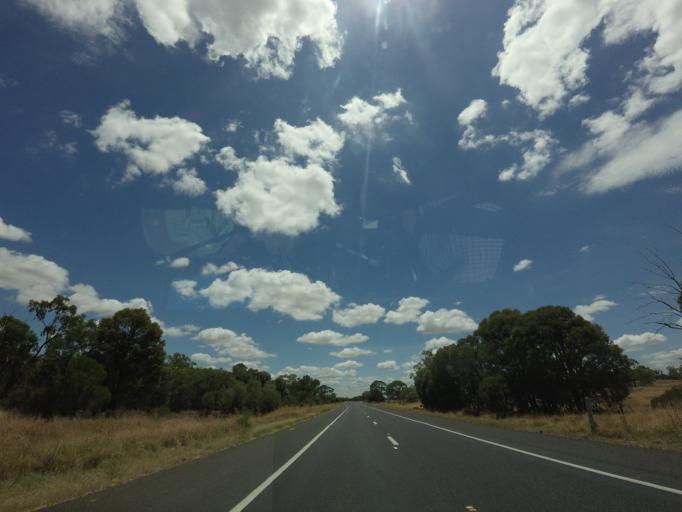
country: AU
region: New South Wales
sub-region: Moree Plains
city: Boggabilla
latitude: -28.8542
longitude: 150.2175
